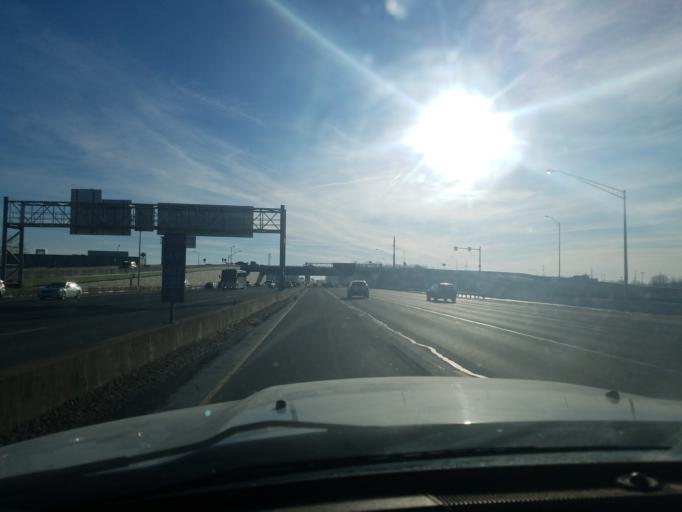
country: US
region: Indiana
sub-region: Hamilton County
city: Fishers
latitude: 39.9439
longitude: -86.0172
